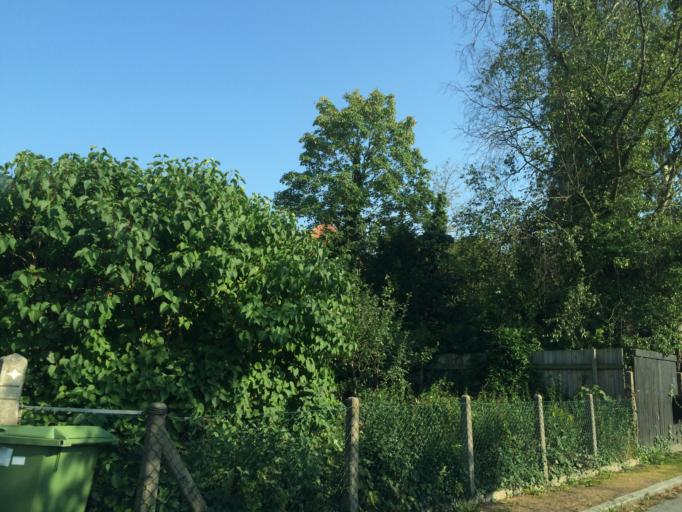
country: SE
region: Skane
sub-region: Malmo
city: Malmoe
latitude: 55.5857
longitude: 12.9599
